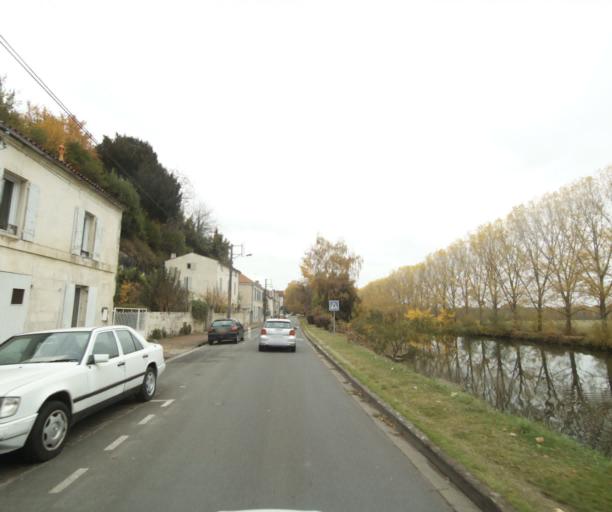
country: FR
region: Poitou-Charentes
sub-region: Departement de la Charente-Maritime
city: Saintes
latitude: 45.7379
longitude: -0.6388
